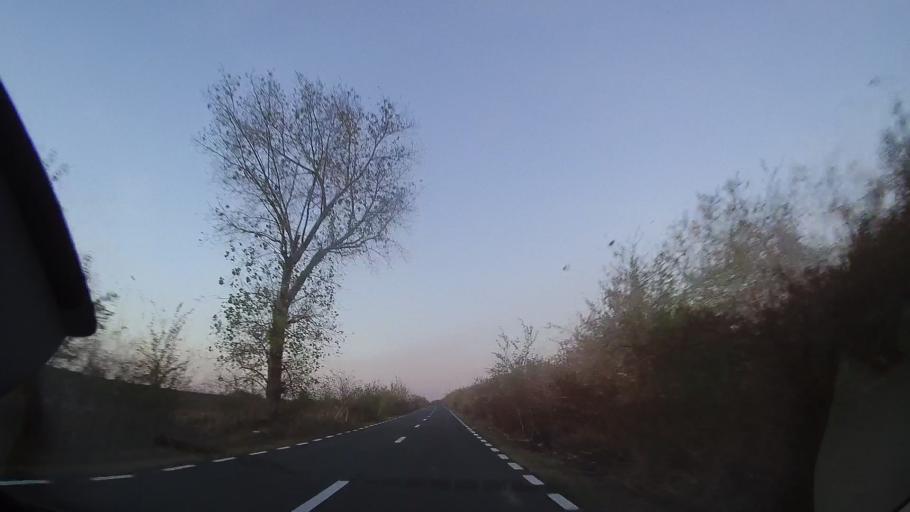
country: RO
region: Constanta
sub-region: Comuna Cobadin
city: Cobadin
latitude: 44.0320
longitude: 28.2608
